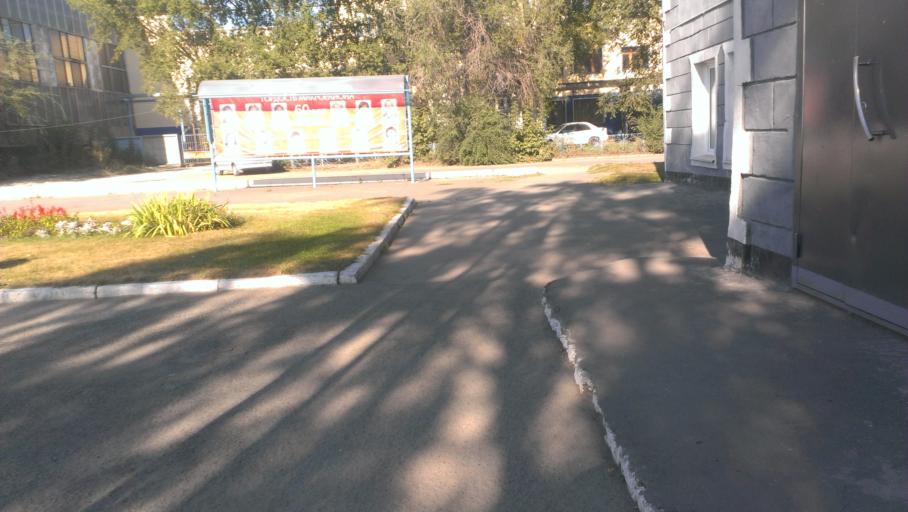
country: RU
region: Altai Krai
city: Novosilikatnyy
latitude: 53.3080
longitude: 83.6228
